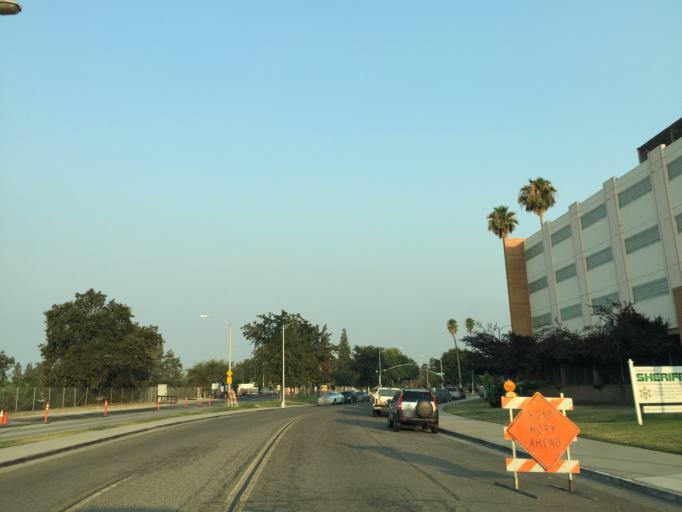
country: US
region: California
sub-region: Tulare County
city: Visalia
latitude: 36.3277
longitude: -119.3167
